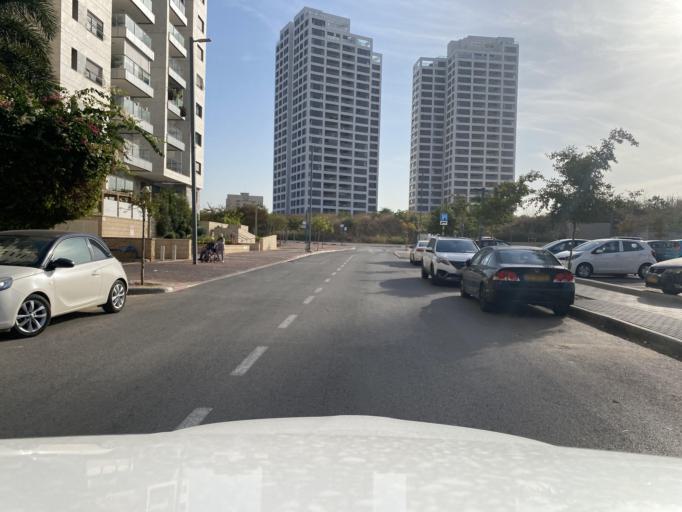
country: IL
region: Tel Aviv
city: Giv`at Shemu'el
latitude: 32.0713
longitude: 34.8548
